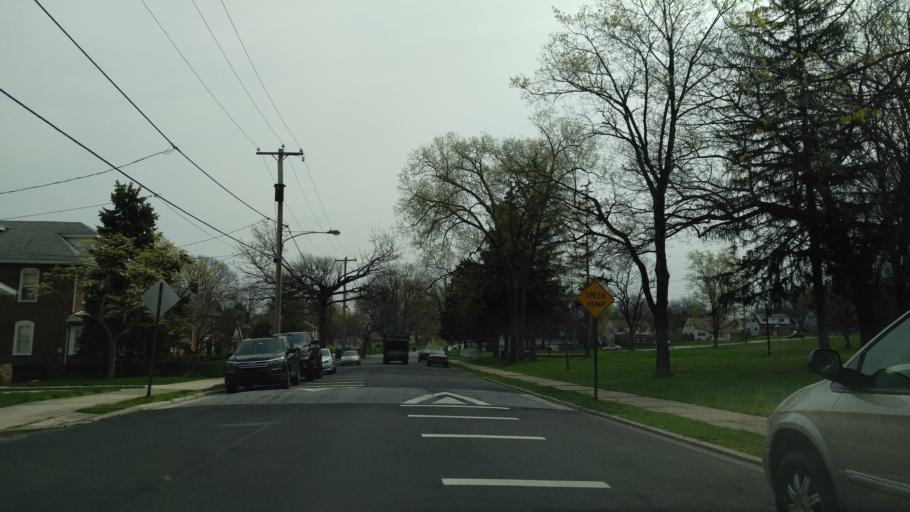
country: US
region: Pennsylvania
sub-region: Chester County
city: Phoenixville
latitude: 40.1289
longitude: -75.5128
